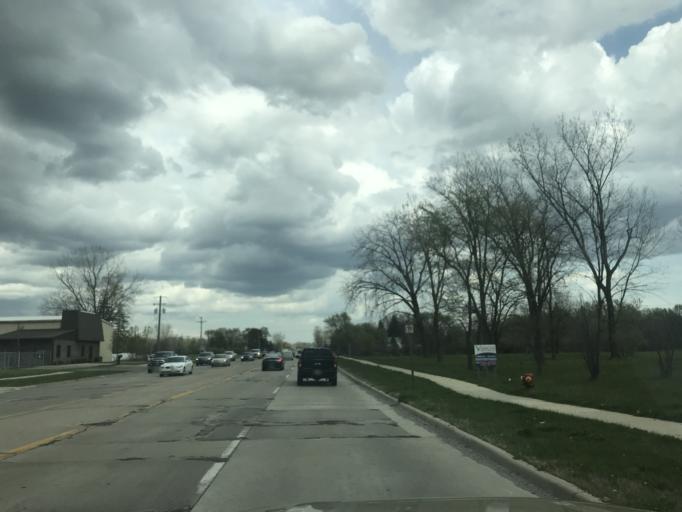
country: US
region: Michigan
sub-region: Wayne County
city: Taylor
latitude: 42.1956
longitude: -83.3204
